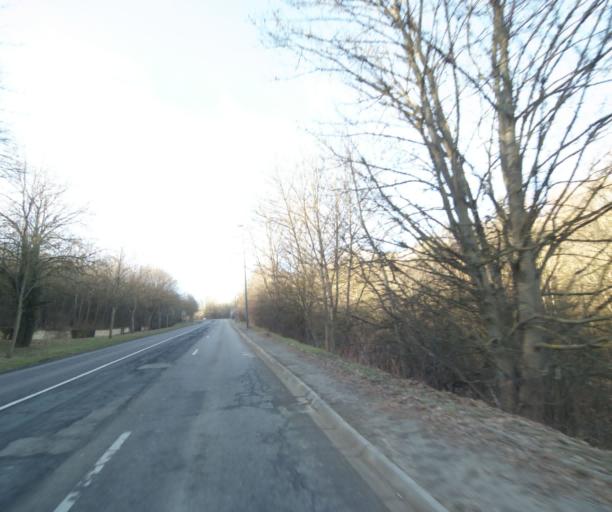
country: FR
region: Lorraine
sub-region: Departement de Meurthe-et-Moselle
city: Villers-les-Nancy
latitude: 48.6660
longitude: 6.1449
